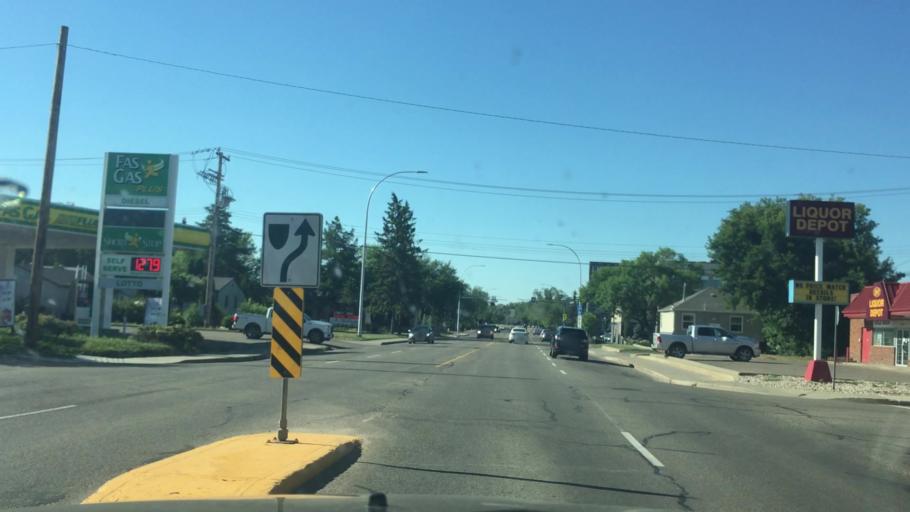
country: CA
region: Alberta
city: Leduc
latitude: 53.2641
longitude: -113.5525
